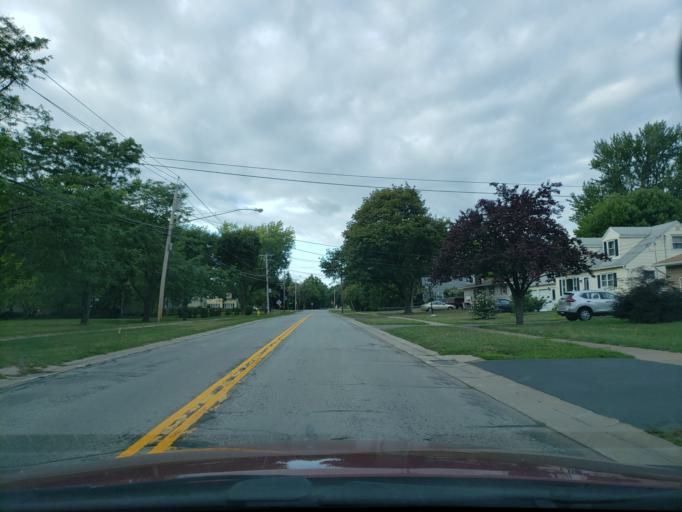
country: US
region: New York
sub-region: Monroe County
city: Greece
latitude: 43.2133
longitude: -77.6516
